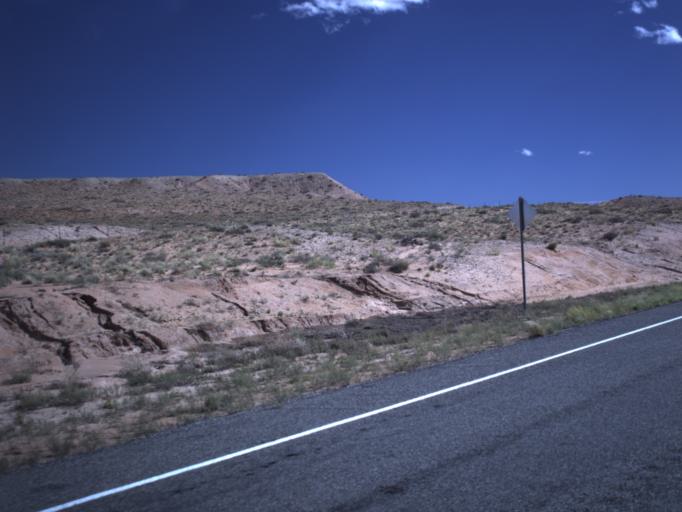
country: US
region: Utah
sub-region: Emery County
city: Ferron
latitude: 38.3176
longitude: -110.6740
